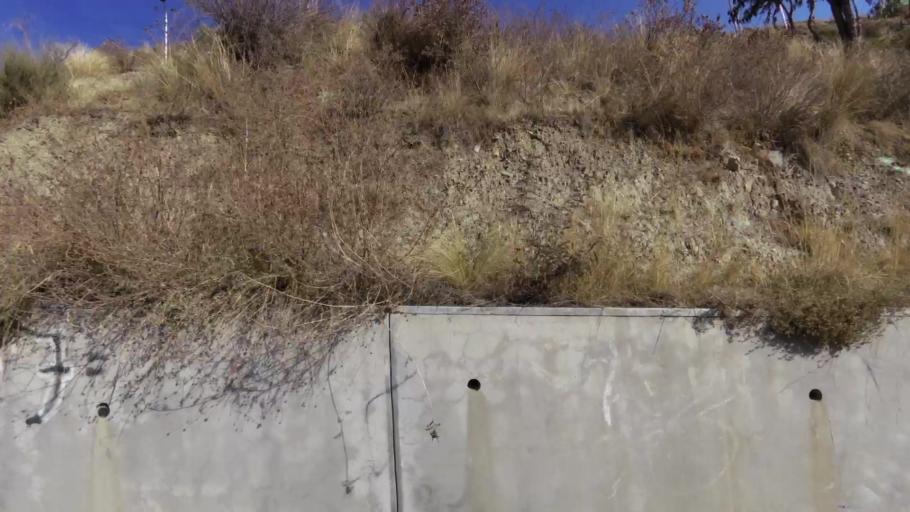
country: BO
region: La Paz
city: La Paz
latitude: -16.5071
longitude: -68.0813
